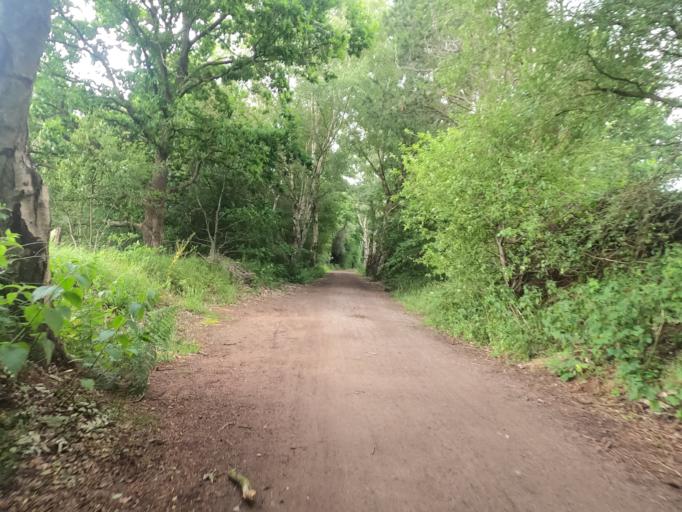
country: GB
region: England
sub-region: Cheshire West and Chester
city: Cuddington
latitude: 53.2334
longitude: -2.6159
